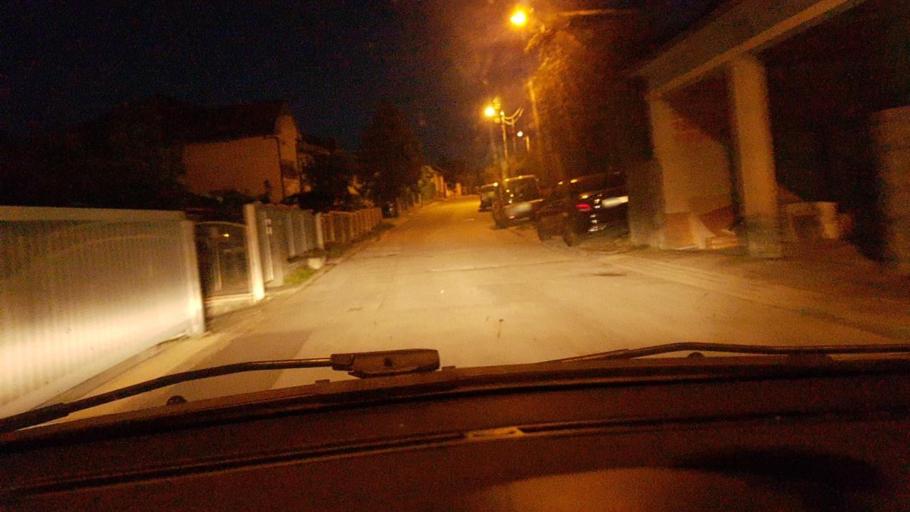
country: HR
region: Zagrebacka
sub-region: Grad Samobor
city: Samobor
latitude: 45.7991
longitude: 15.7108
